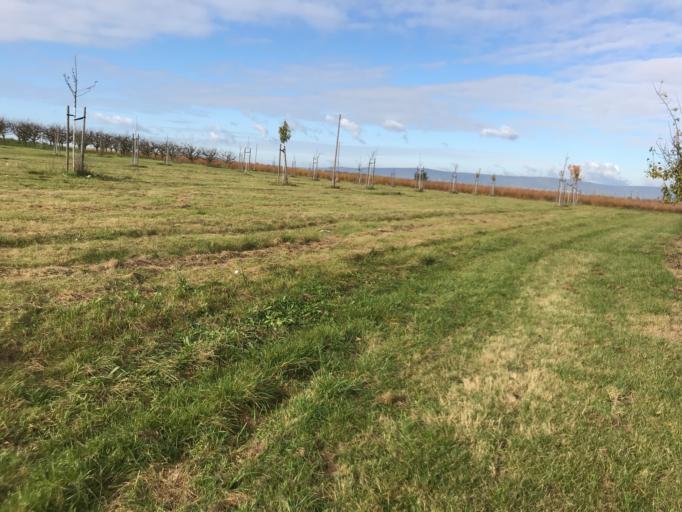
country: DE
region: Rheinland-Pfalz
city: Budenheim
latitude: 49.9859
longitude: 8.1508
